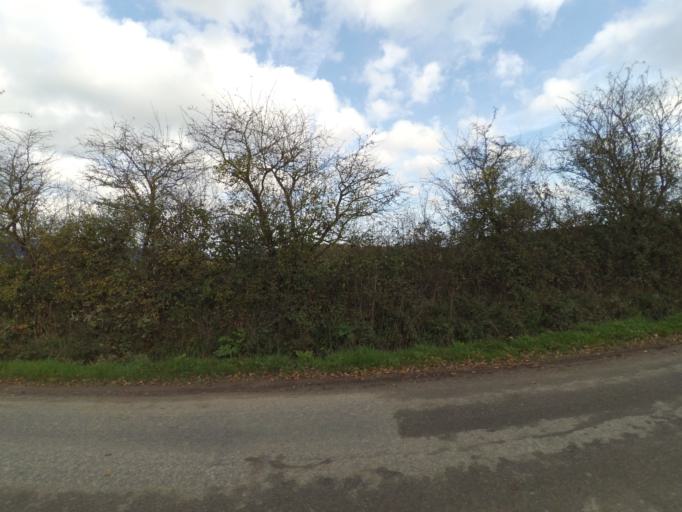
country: FR
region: Pays de la Loire
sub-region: Departement de la Vendee
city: Saint-Hilaire-de-Loulay
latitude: 47.0185
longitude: -1.3551
